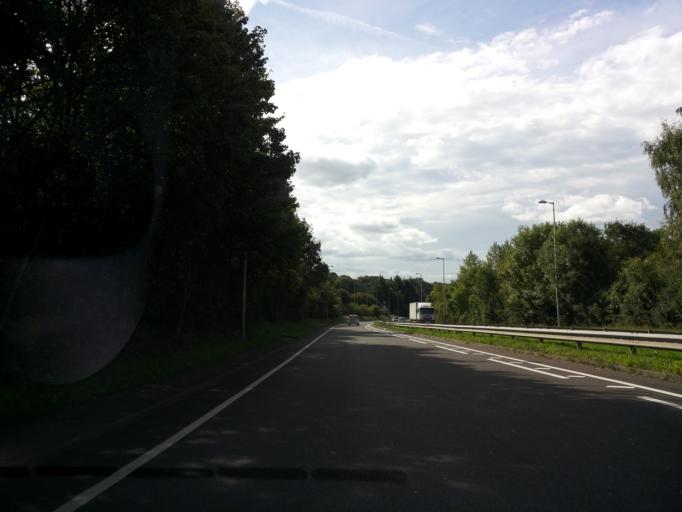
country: GB
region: England
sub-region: Kent
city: Halstead
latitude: 51.3456
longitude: 0.1240
